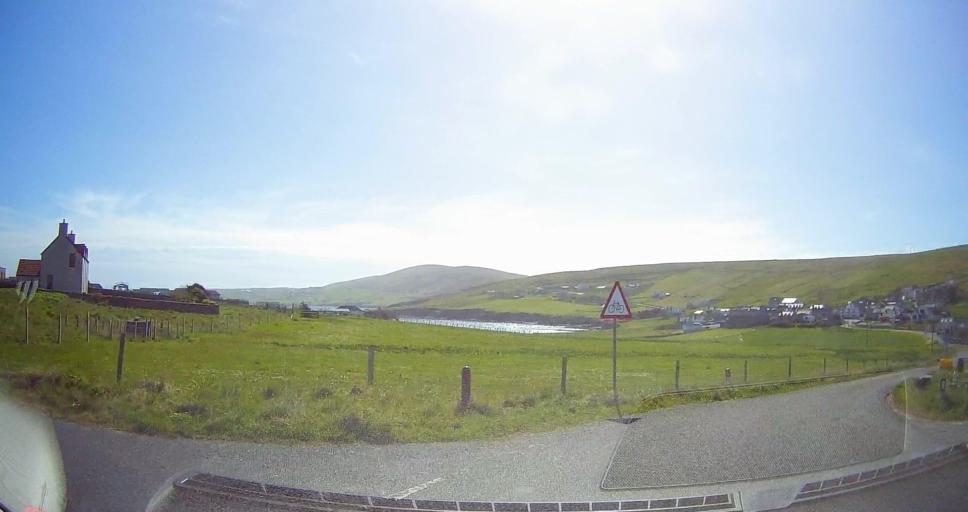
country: GB
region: Scotland
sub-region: Shetland Islands
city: Sandwick
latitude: 59.9993
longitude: -1.2474
